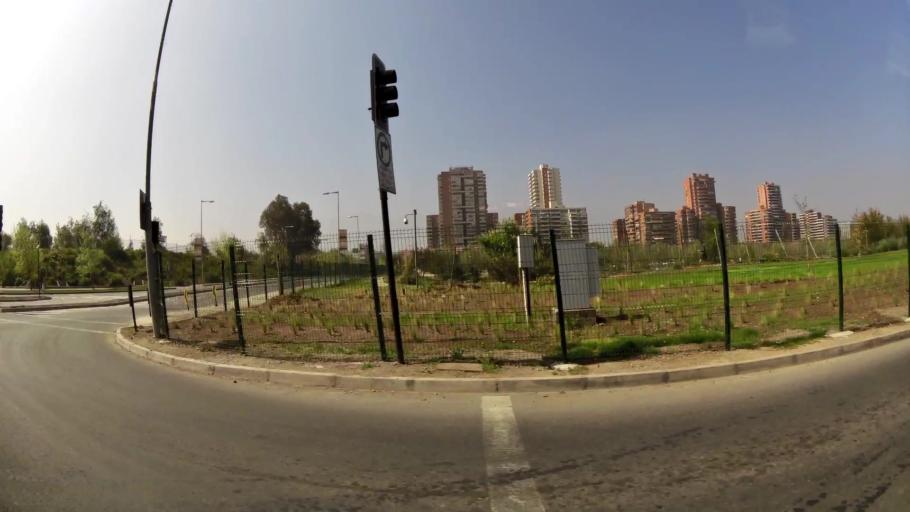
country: CL
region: Santiago Metropolitan
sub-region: Provincia de Santiago
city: Villa Presidente Frei, Nunoa, Santiago, Chile
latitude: -33.3935
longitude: -70.6016
